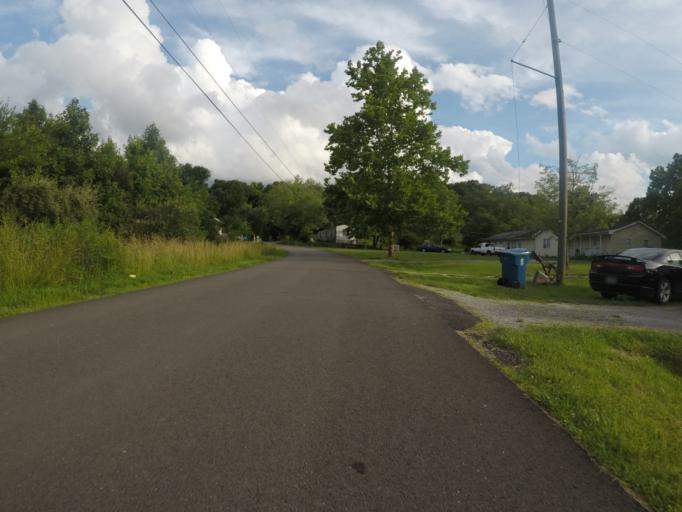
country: US
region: West Virginia
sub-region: Cabell County
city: Pea Ridge
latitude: 38.4041
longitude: -82.3587
